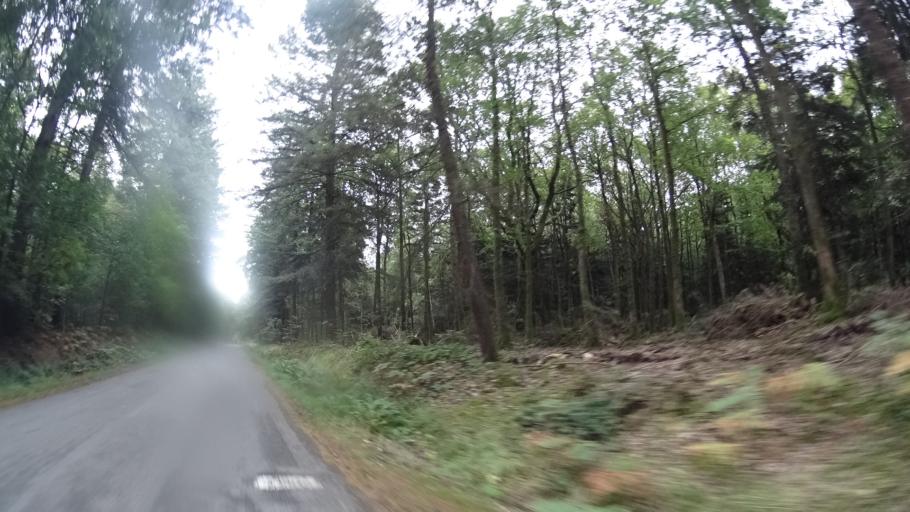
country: FR
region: Brittany
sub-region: Departement d'Ille-et-Vilaine
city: Paimpont
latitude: 48.0739
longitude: -2.1670
